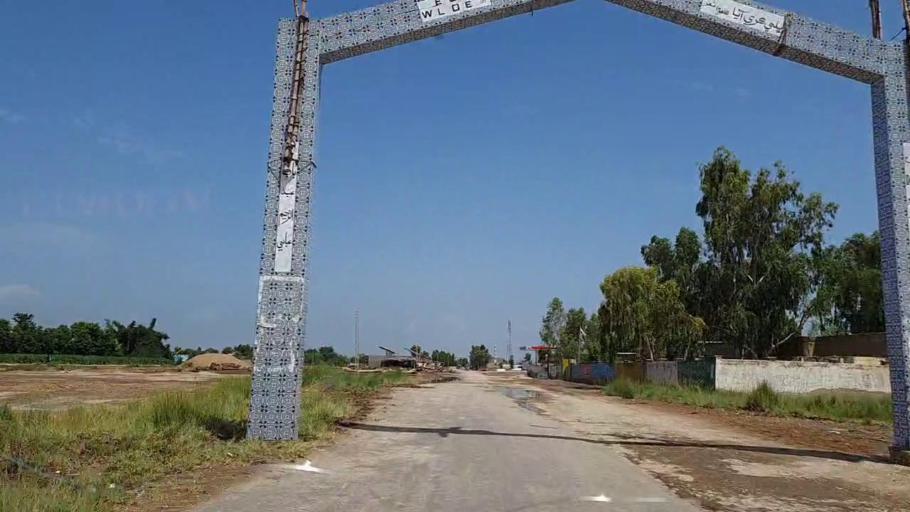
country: PK
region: Sindh
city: Naushahro Firoz
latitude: 26.8127
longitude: 68.1911
